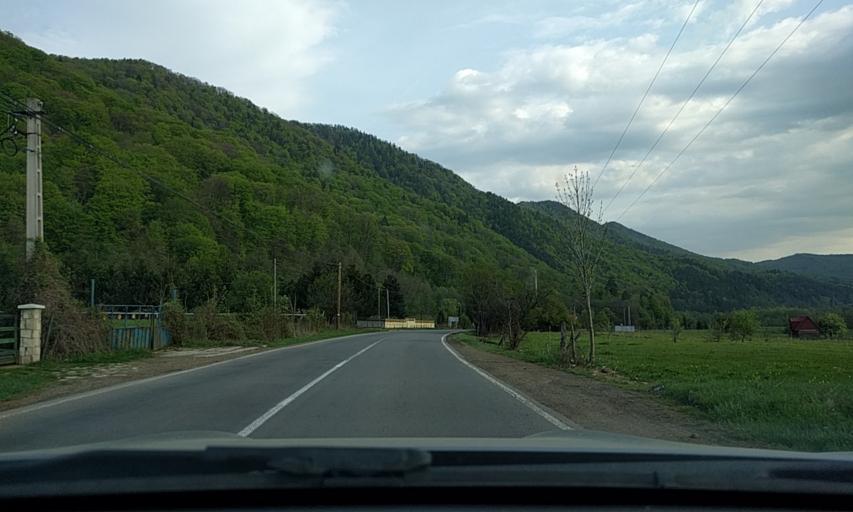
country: RO
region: Bacau
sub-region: Oras Slanic-Moldova
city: Slanic-Moldova
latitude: 46.1507
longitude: 26.4591
